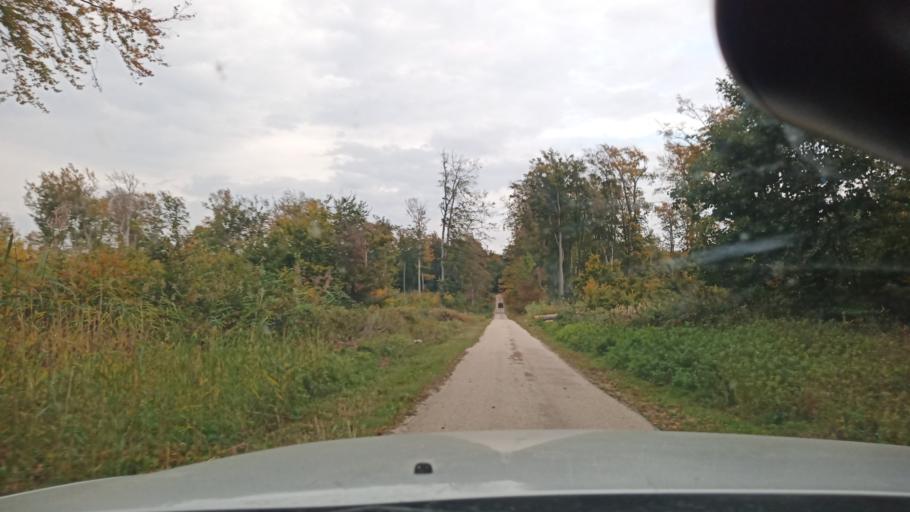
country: HU
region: Fejer
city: Pusztavam
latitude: 47.3927
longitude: 18.2918
